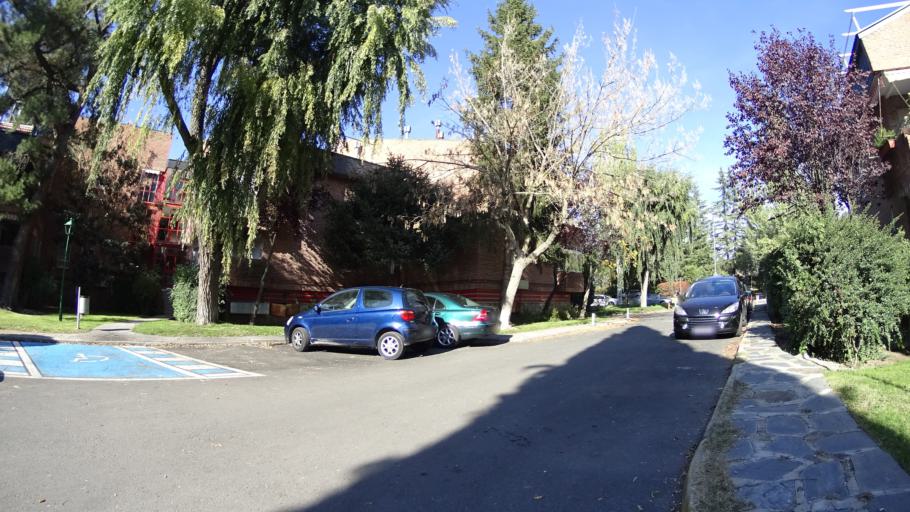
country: ES
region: Madrid
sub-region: Provincia de Madrid
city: Navalquejigo
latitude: 40.6052
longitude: -4.0244
